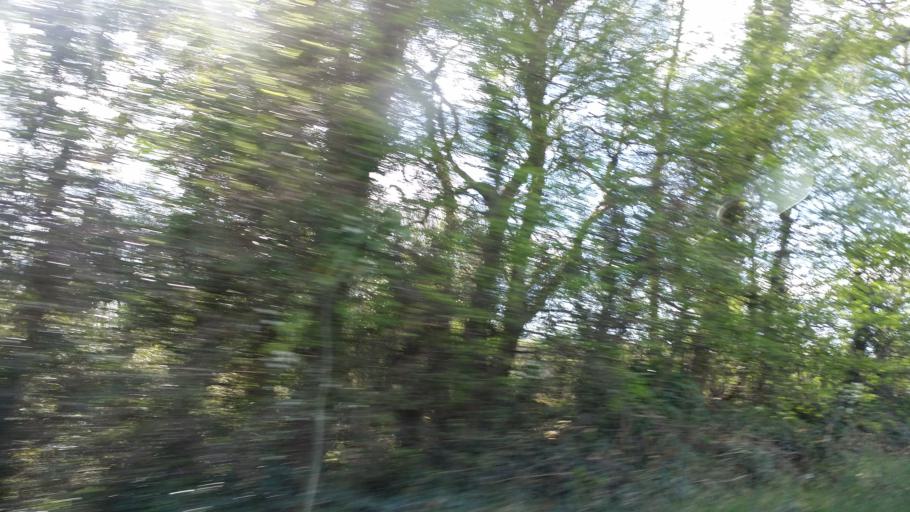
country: IE
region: Ulster
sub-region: County Donegal
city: Ballyshannon
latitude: 54.4796
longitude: -8.1057
